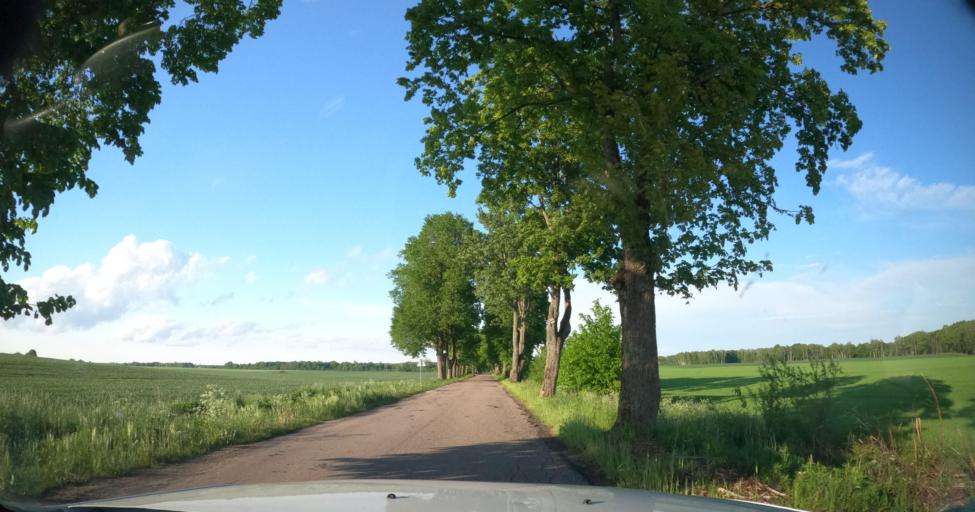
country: PL
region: Warmian-Masurian Voivodeship
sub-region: Powiat braniewski
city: Braniewo
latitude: 54.2741
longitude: 19.8366
